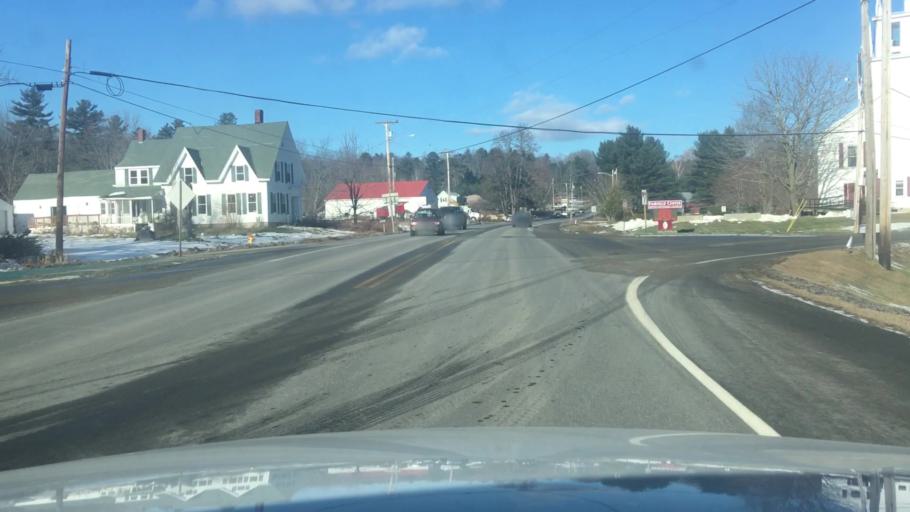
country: US
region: Maine
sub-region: Kennebec County
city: Waterville
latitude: 44.6066
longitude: -69.6623
